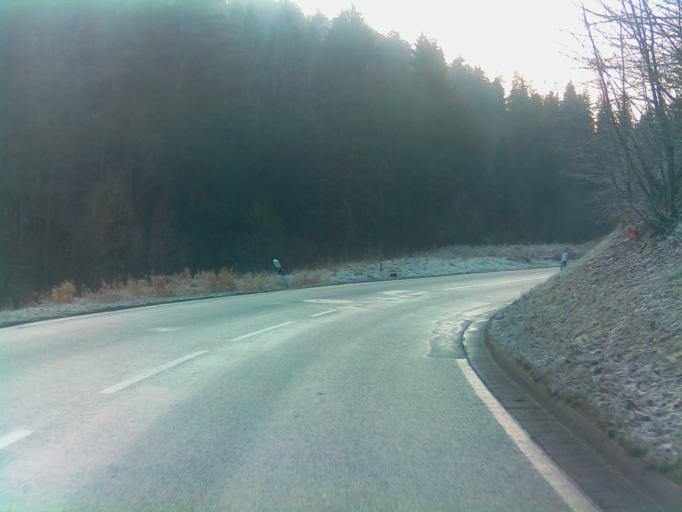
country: DE
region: Thuringia
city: Judenbach
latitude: 50.3816
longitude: 11.2192
